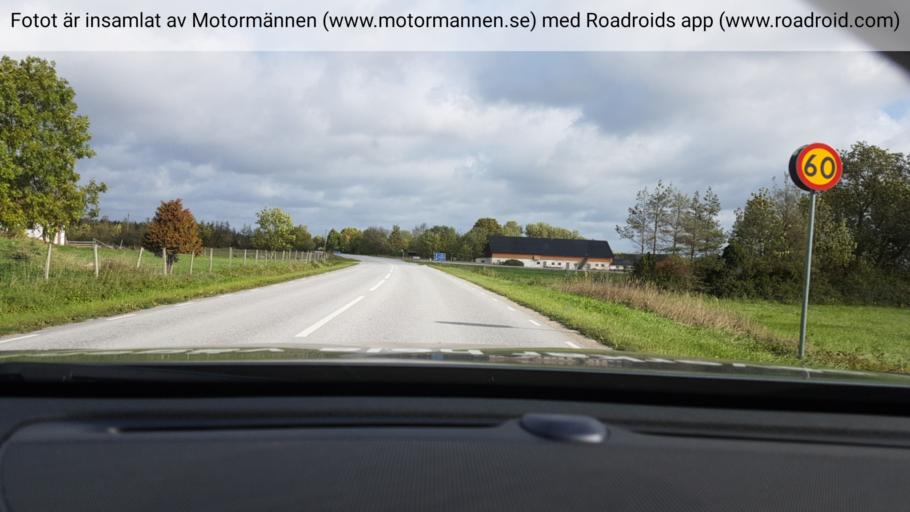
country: SE
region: Gotland
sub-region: Gotland
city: Slite
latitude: 57.7719
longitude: 18.7764
